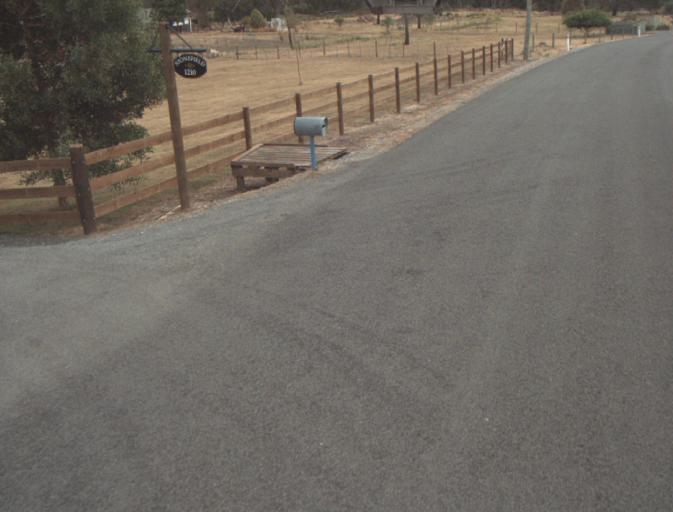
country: AU
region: Tasmania
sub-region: Launceston
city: Mayfield
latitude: -41.2825
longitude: 147.0329
